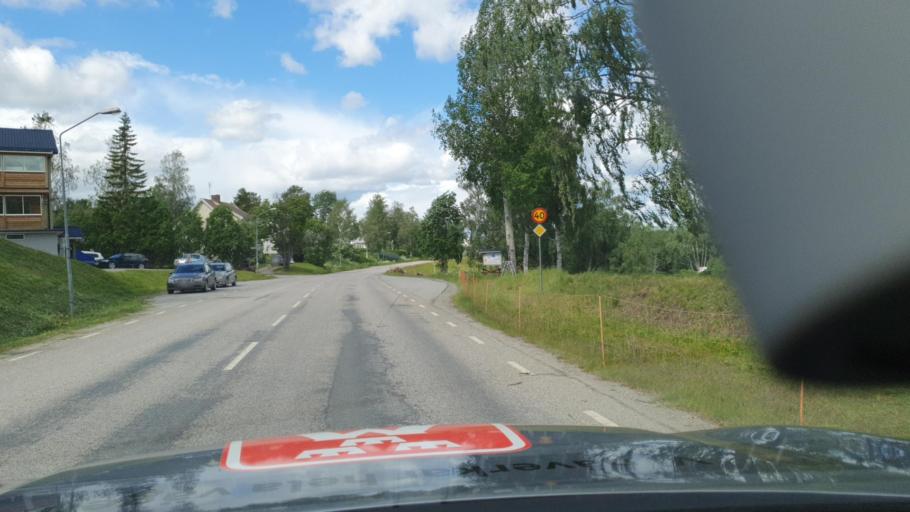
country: SE
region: Vaesternorrland
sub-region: OErnskoeldsviks Kommun
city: Bjasta
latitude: 63.2933
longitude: 18.2928
